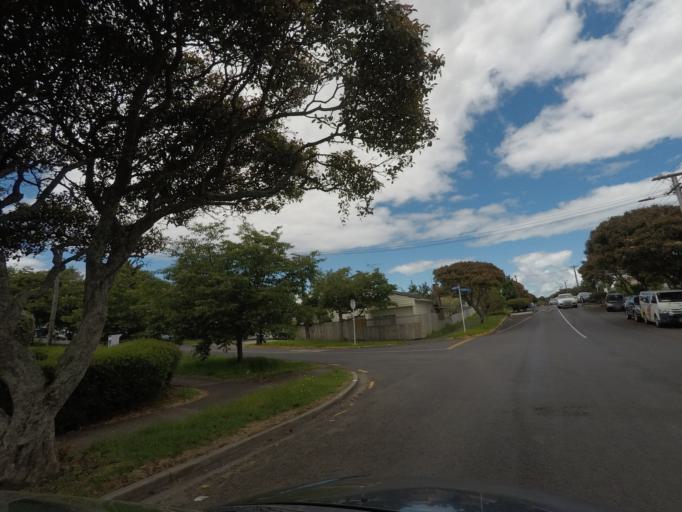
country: NZ
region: Auckland
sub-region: Auckland
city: Auckland
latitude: -36.8858
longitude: 174.7350
